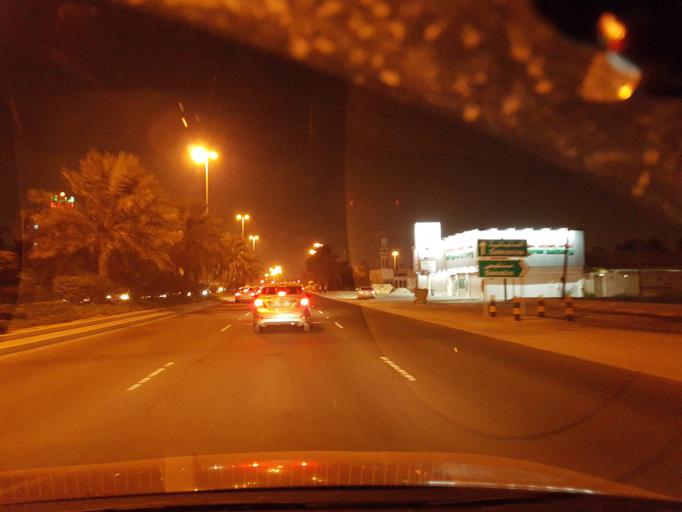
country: BH
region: Manama
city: Jidd Hafs
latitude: 26.2258
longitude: 50.5614
